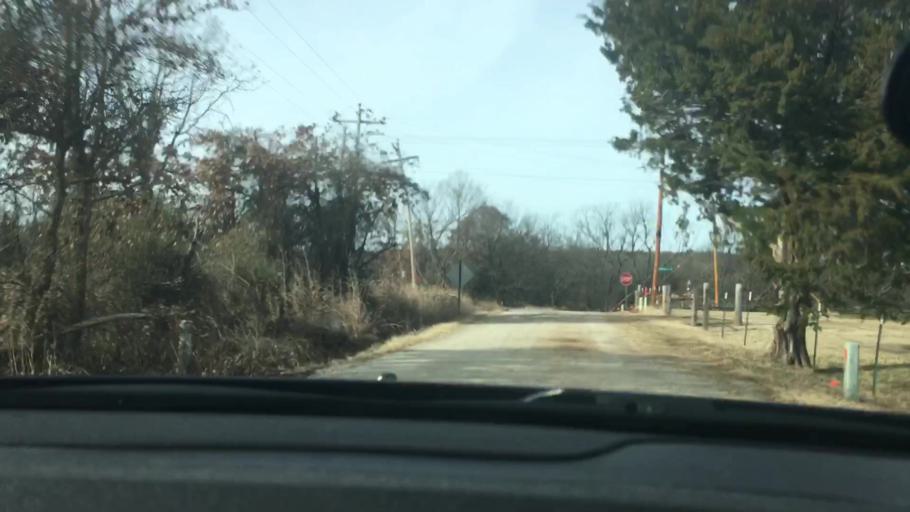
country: US
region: Oklahoma
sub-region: Garvin County
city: Wynnewood
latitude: 34.6374
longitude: -97.2468
